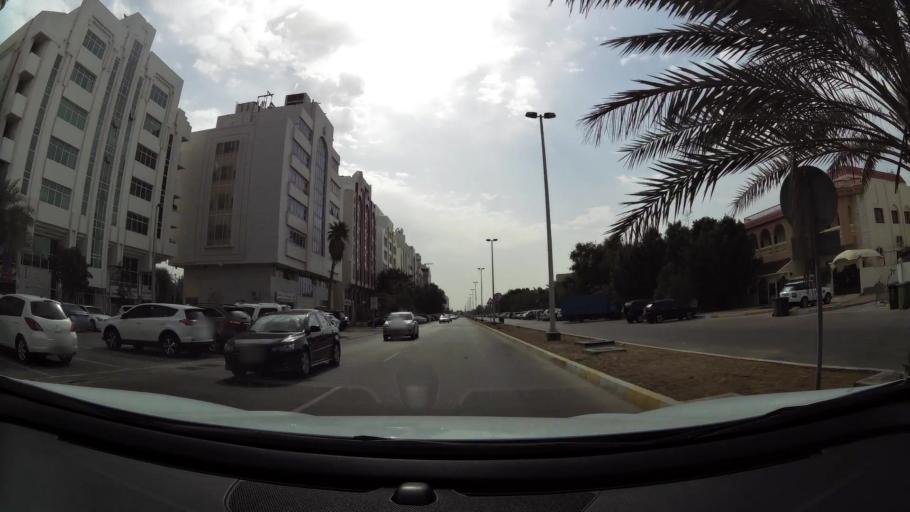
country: AE
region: Abu Dhabi
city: Abu Dhabi
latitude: 24.4540
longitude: 54.3846
